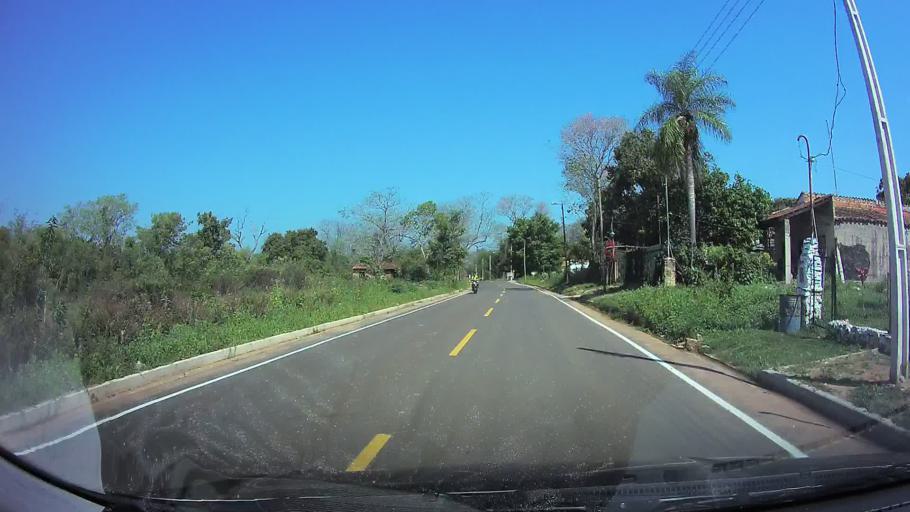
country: PY
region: Central
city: Limpio
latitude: -25.2397
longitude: -57.4958
